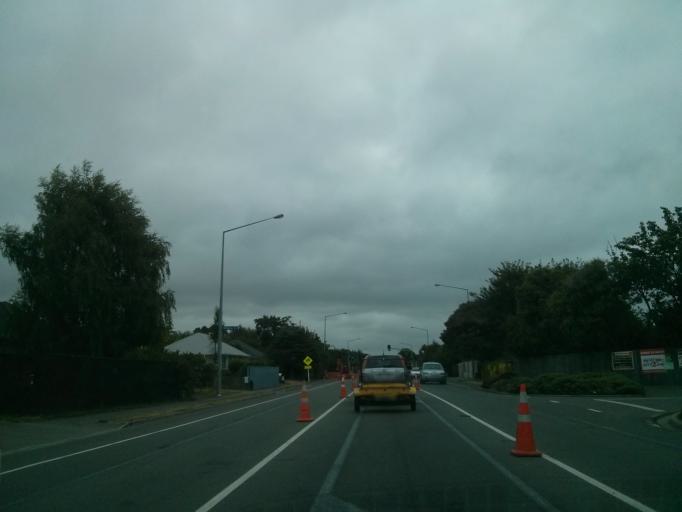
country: NZ
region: Canterbury
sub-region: Christchurch City
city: Christchurch
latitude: -43.5370
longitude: 172.5681
